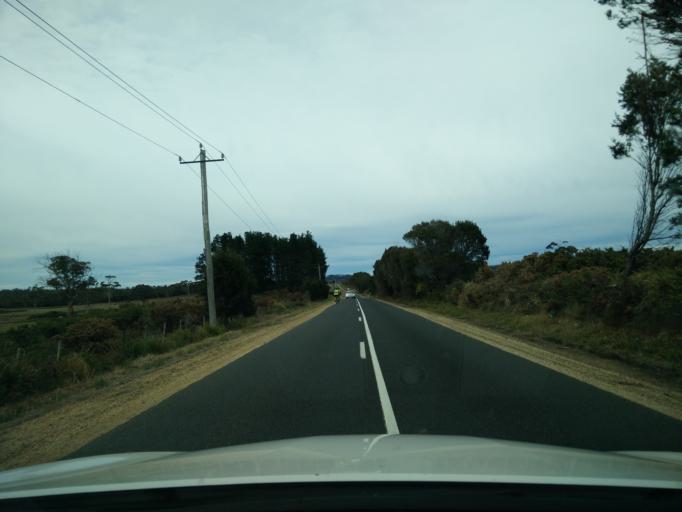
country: AU
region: Tasmania
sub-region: Break O'Day
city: St Helens
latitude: -41.9332
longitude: 148.2257
